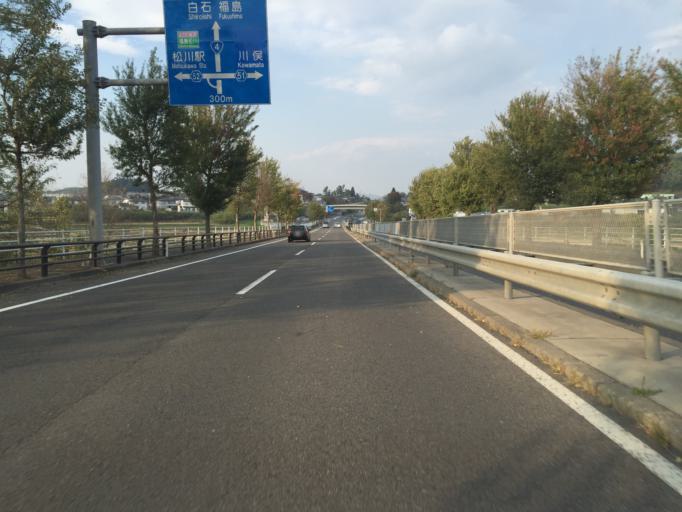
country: JP
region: Fukushima
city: Nihommatsu
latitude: 37.6474
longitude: 140.4872
